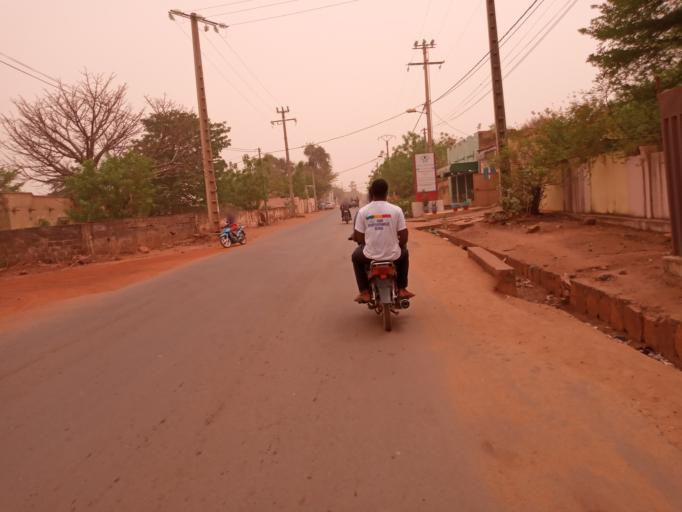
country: ML
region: Koulikoro
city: Koulikoro
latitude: 12.8587
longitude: -7.5602
